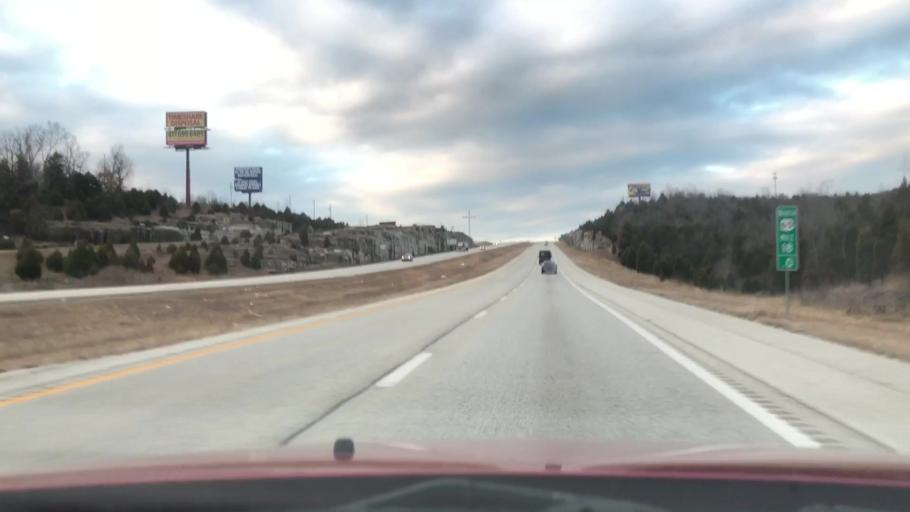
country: US
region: Missouri
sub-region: Taney County
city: Merriam Woods
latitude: 36.7385
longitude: -93.2214
